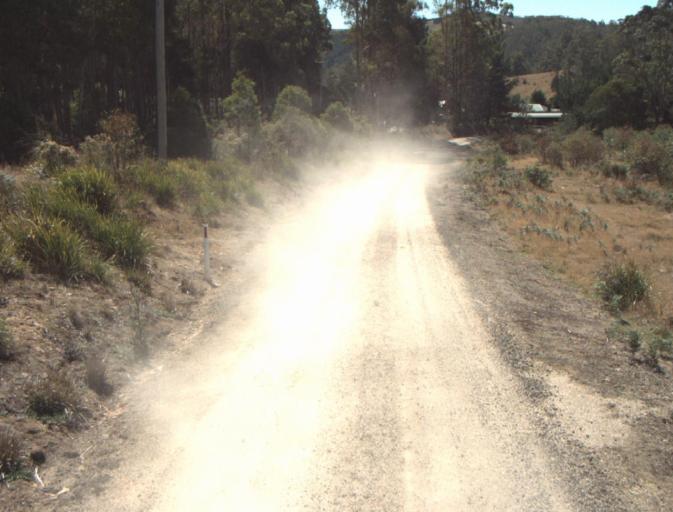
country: AU
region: Tasmania
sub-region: Dorset
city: Scottsdale
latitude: -41.3163
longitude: 147.3817
